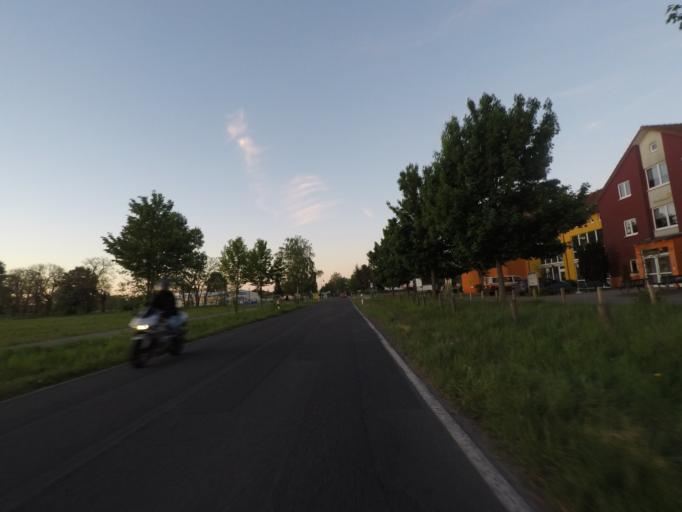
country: DE
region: Brandenburg
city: Britz
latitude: 52.8611
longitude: 13.7439
